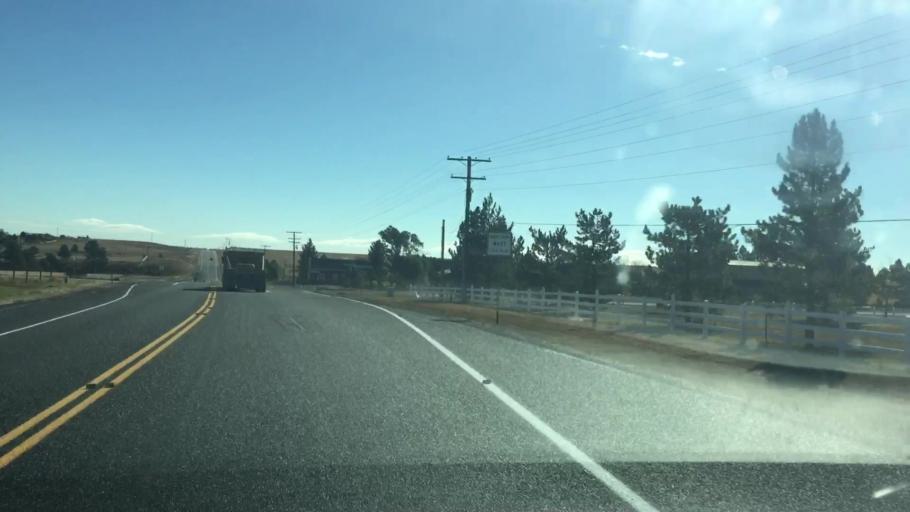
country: US
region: Colorado
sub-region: Elbert County
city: Ponderosa Park
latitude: 39.3619
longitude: -104.6677
